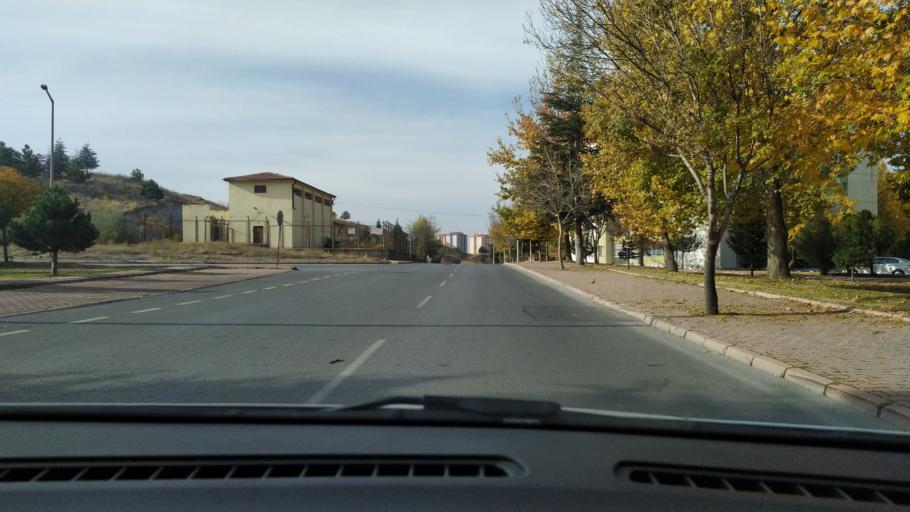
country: TR
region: Kayseri
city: Melikgazi
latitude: 38.7364
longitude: 35.3891
